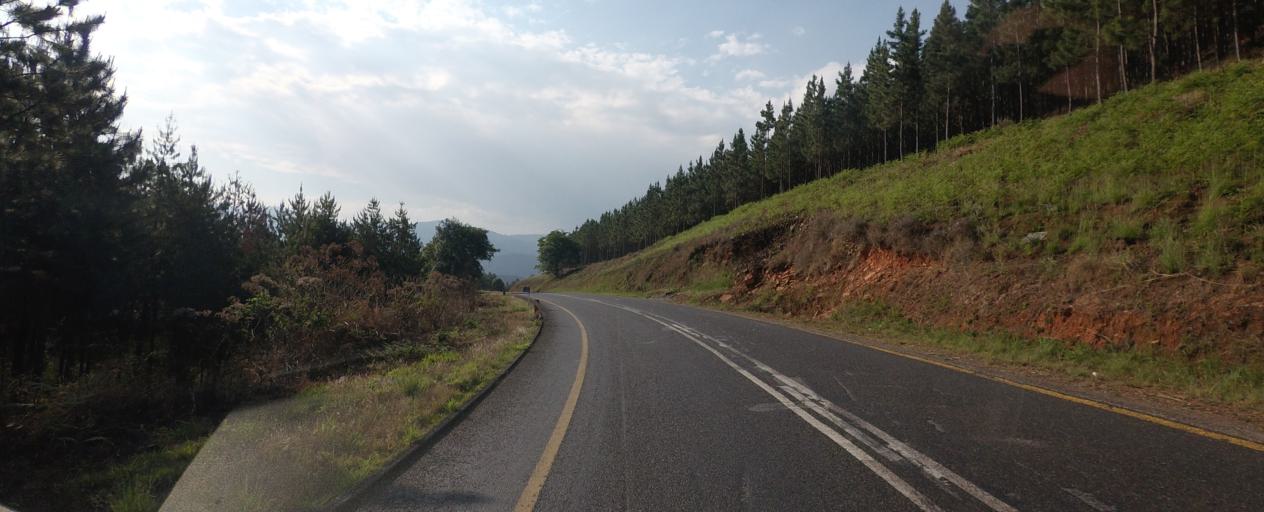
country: ZA
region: Mpumalanga
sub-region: Ehlanzeni District
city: Graksop
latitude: -25.1634
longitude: 30.7318
